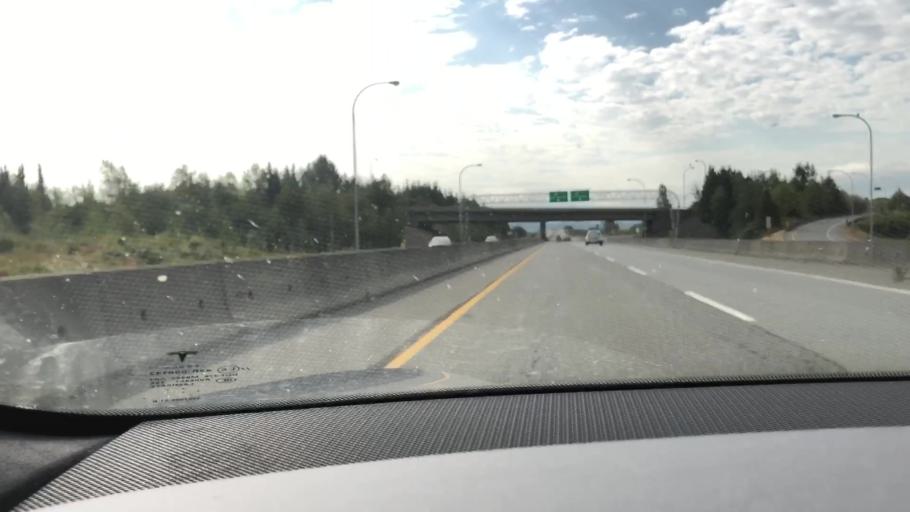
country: CA
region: British Columbia
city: Delta
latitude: 49.1042
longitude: -122.9015
